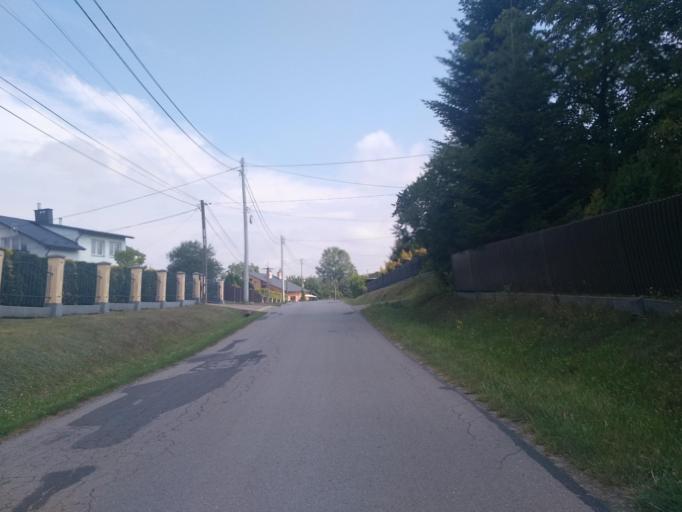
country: PL
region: Subcarpathian Voivodeship
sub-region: Powiat lancucki
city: Kraczkowa
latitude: 50.0370
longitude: 22.1761
